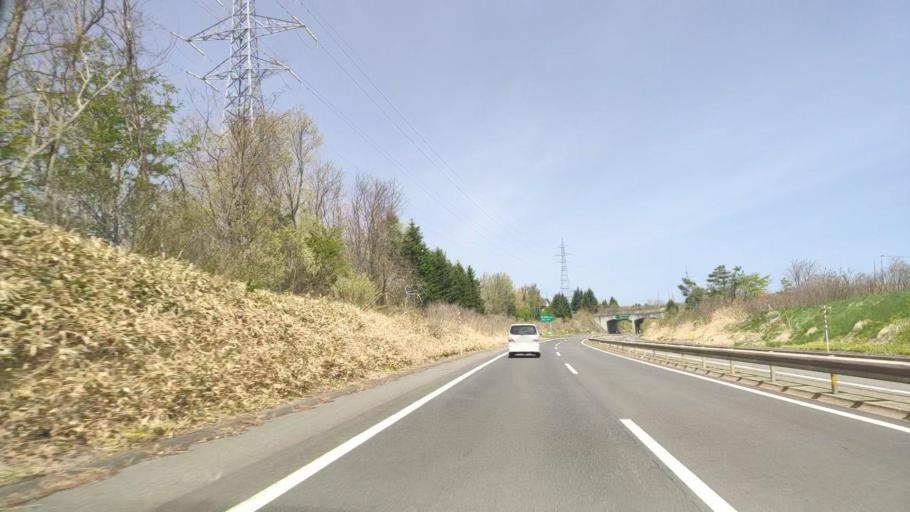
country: JP
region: Aomori
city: Hachinohe
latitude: 40.4756
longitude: 141.4600
